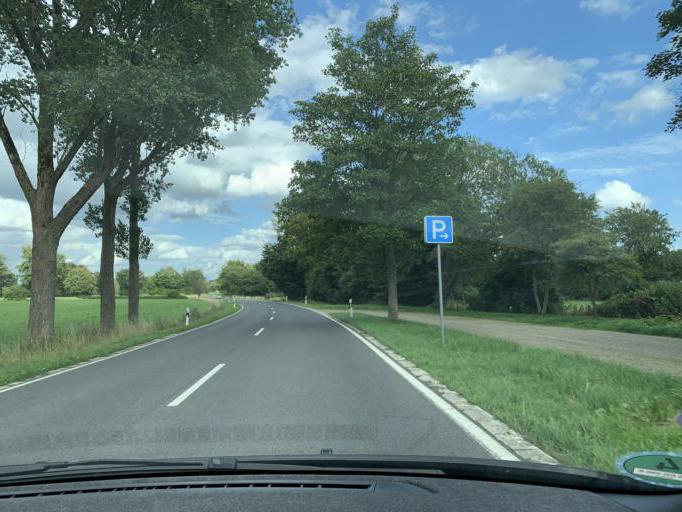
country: DE
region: North Rhine-Westphalia
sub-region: Regierungsbezirk Koln
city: Simmerath
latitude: 50.5941
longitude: 6.2699
